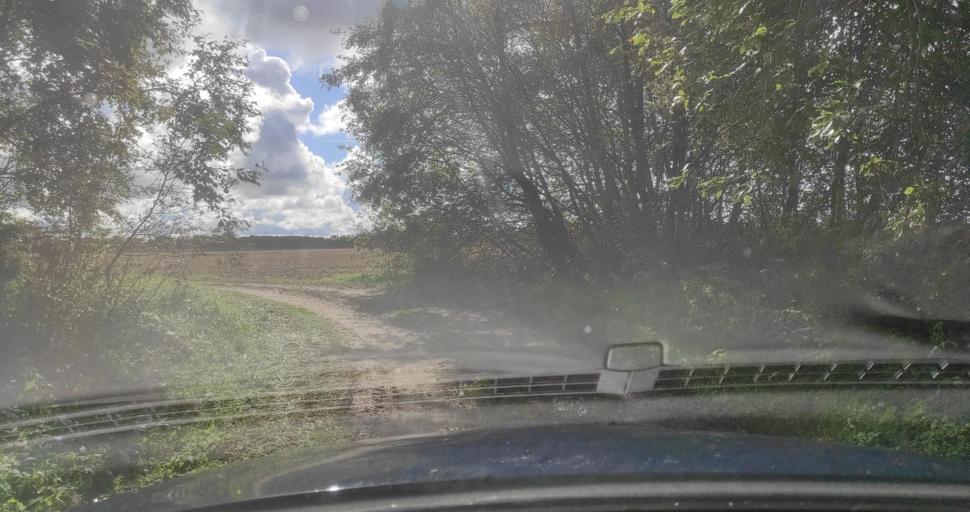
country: LV
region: Ventspils Rajons
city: Piltene
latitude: 57.2692
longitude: 21.6032
